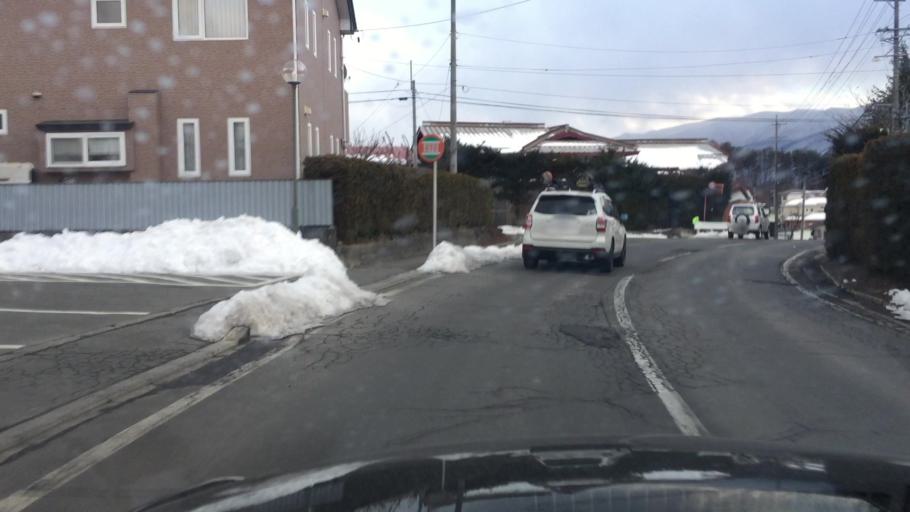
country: JP
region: Nagano
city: Chino
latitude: 35.9619
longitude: 138.2162
